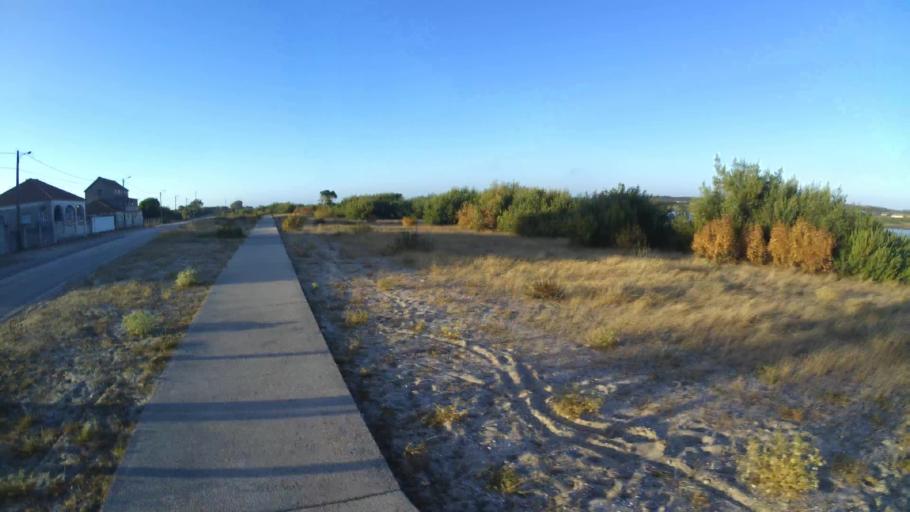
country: PT
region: Aveiro
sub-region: Ilhavo
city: Gafanha da Encarnacao
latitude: 40.5705
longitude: -8.7564
